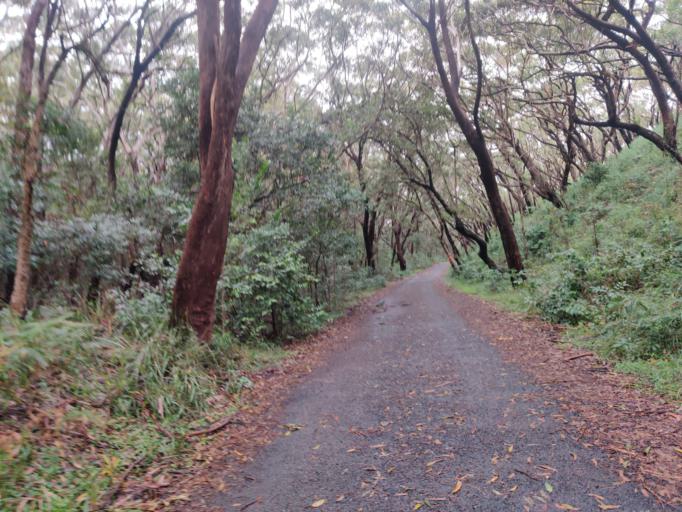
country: AU
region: New South Wales
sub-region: Great Lakes
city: Forster
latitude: -32.4377
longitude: 152.5366
